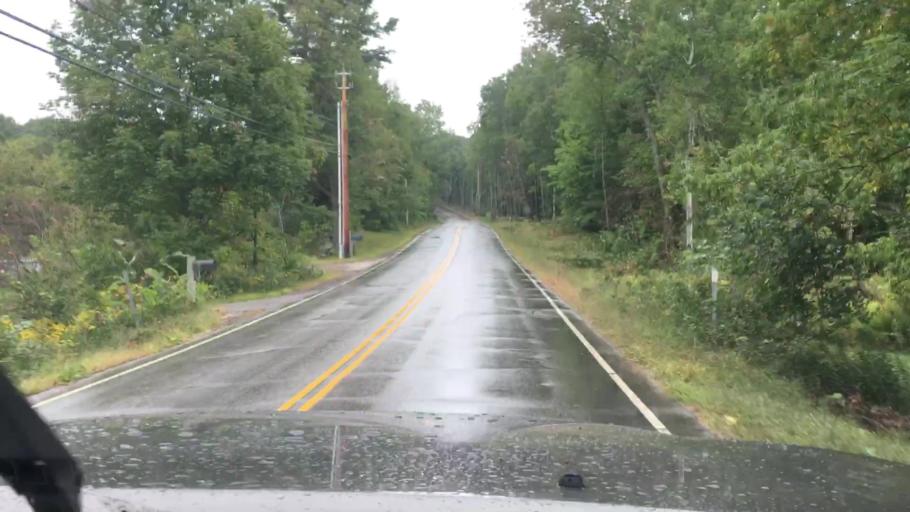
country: US
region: New Hampshire
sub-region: Belknap County
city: Meredith
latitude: 43.6527
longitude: -71.5476
